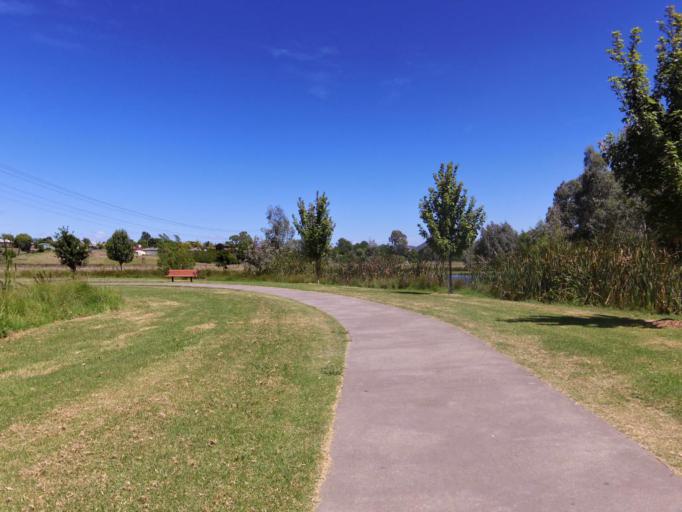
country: AU
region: Victoria
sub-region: Wodonga
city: Wodonga
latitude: -36.1134
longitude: 146.8866
